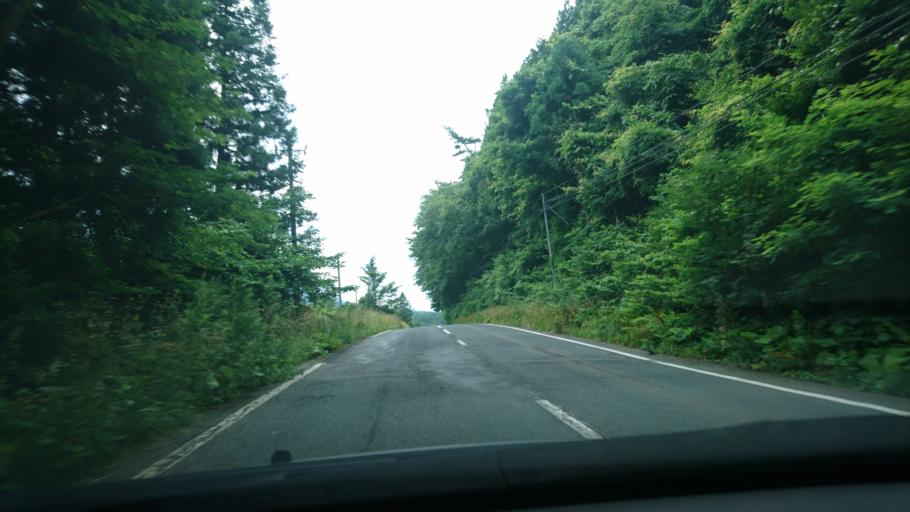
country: JP
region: Iwate
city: Ichinoseki
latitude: 38.8825
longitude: 141.4251
